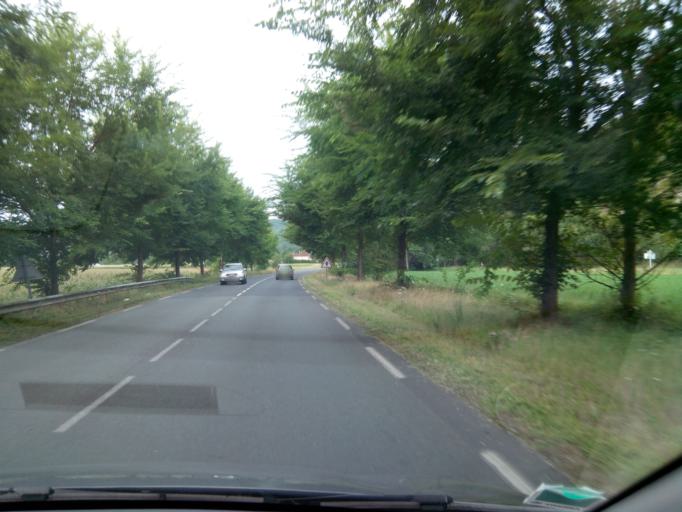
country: FR
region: Aquitaine
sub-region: Departement de la Dordogne
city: Eyvigues-et-Eybenes
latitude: 44.8886
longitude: 1.3974
